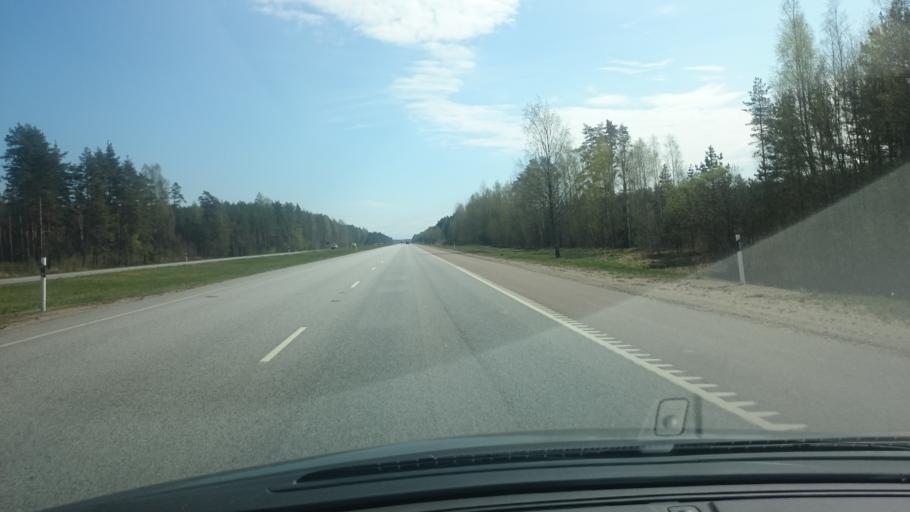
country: EE
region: Harju
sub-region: Kuusalu vald
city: Kuusalu
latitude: 59.4510
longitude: 25.4632
